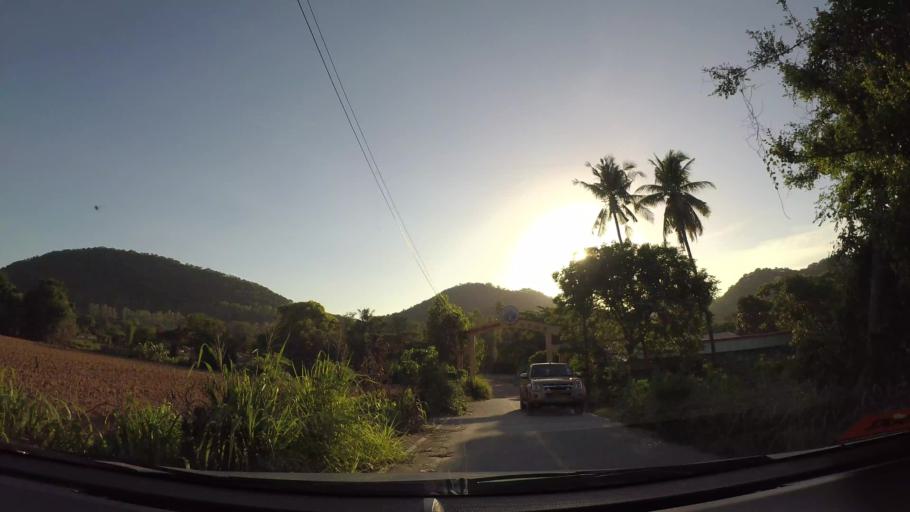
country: TH
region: Chon Buri
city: Si Racha
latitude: 13.1377
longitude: 100.9309
